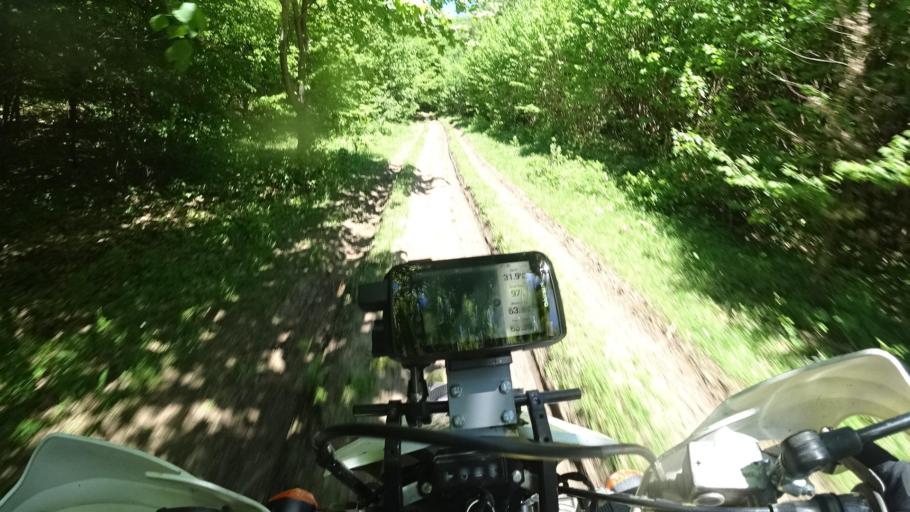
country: BA
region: Republika Srpska
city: Skender Vakuf
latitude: 44.4886
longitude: 17.2373
